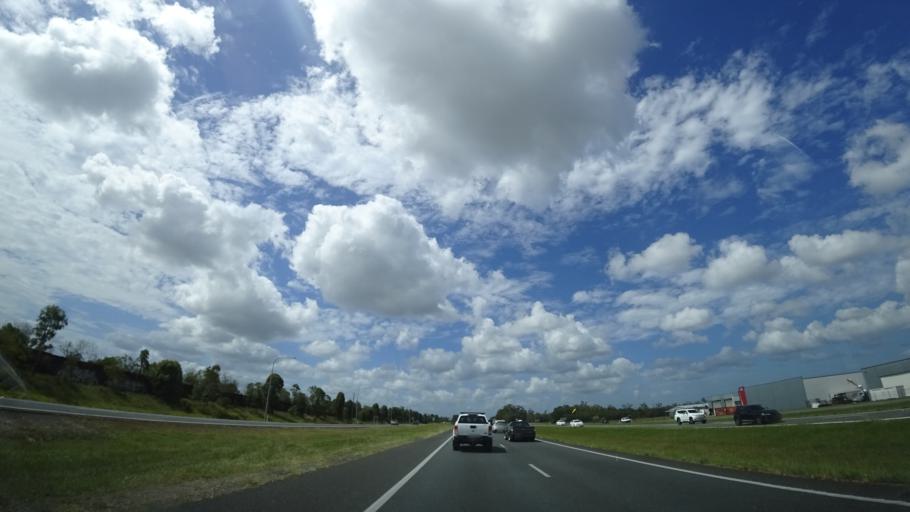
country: AU
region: Queensland
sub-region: Moreton Bay
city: Caboolture
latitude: -27.0801
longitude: 152.9757
